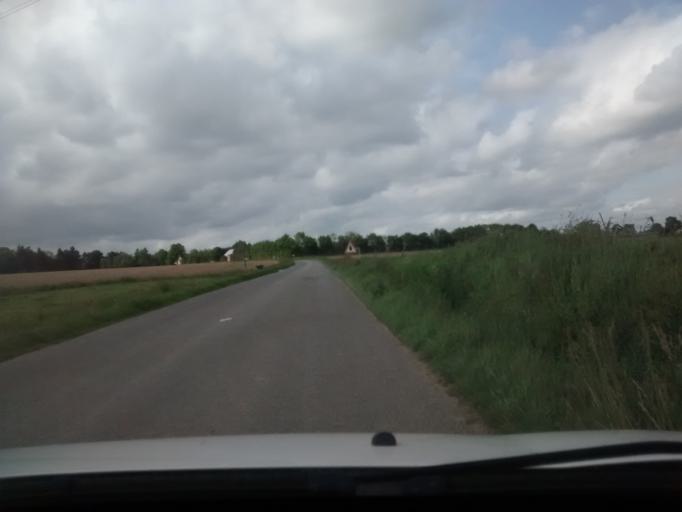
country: FR
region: Brittany
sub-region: Departement d'Ille-et-Vilaine
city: Noyal-sur-Vilaine
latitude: 48.0817
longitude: -1.5464
